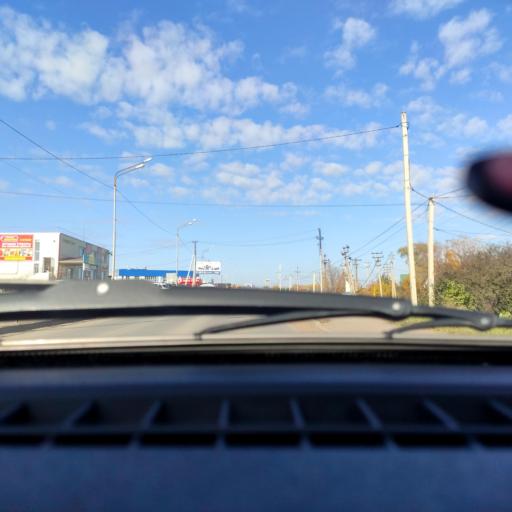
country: RU
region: Bashkortostan
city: Ufa
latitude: 54.6145
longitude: 55.9357
